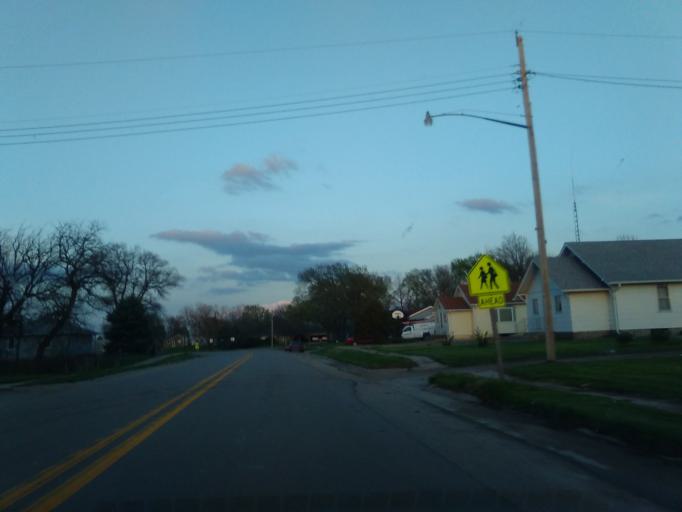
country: US
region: Nebraska
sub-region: Nuckolls County
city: Nelson
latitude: 40.2920
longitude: -98.2582
